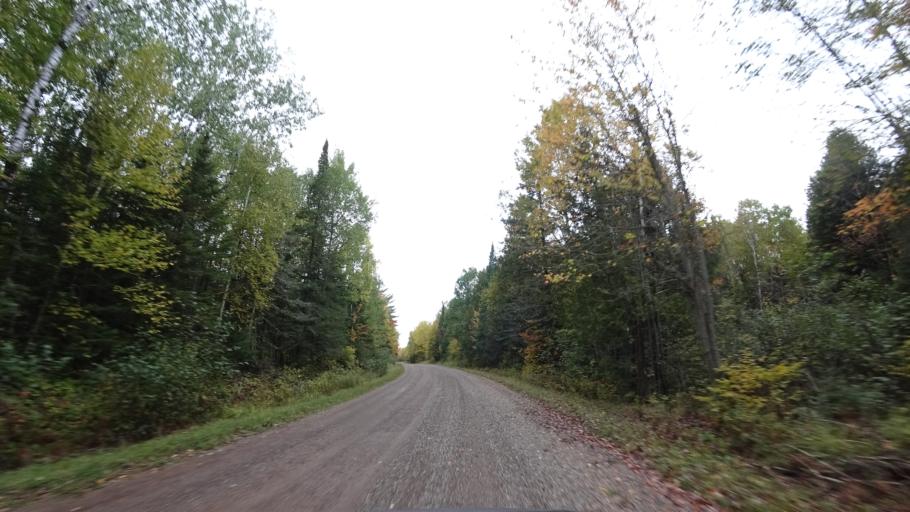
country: US
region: Wisconsin
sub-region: Sawyer County
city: Little Round Lake
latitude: 45.9702
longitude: -90.9807
